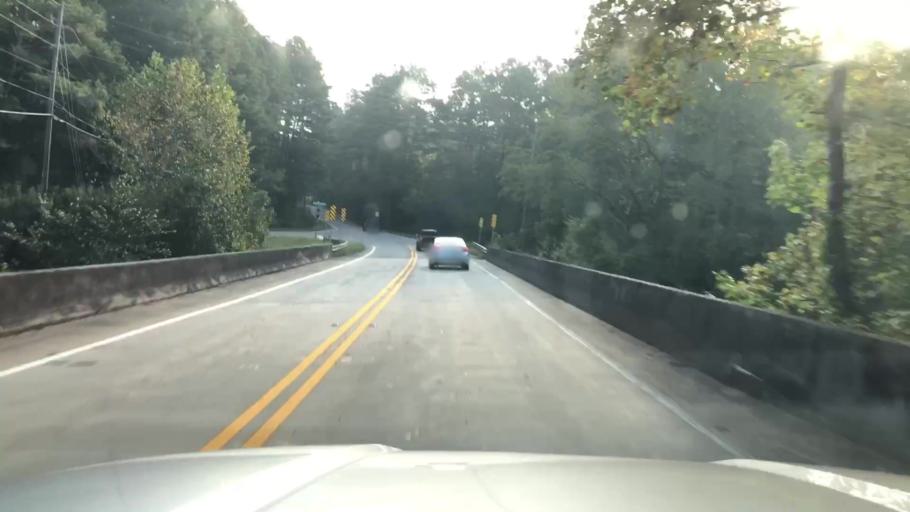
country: US
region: Georgia
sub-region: Bartow County
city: Emerson
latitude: 34.0788
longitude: -84.7545
